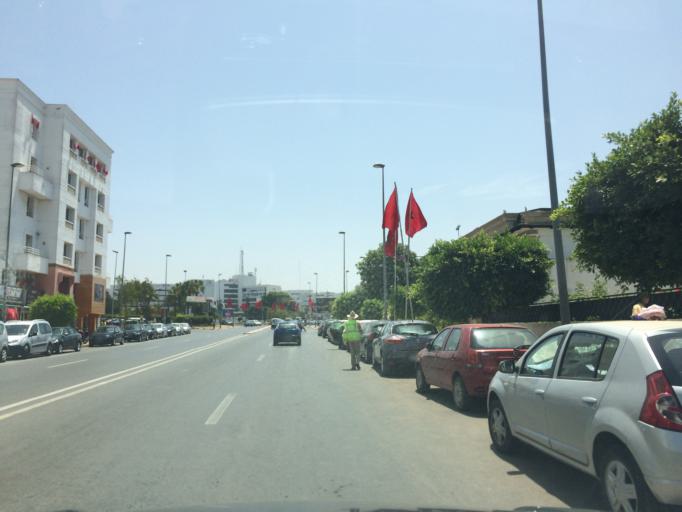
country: MA
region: Rabat-Sale-Zemmour-Zaer
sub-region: Rabat
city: Rabat
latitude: 33.9883
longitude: -6.8516
